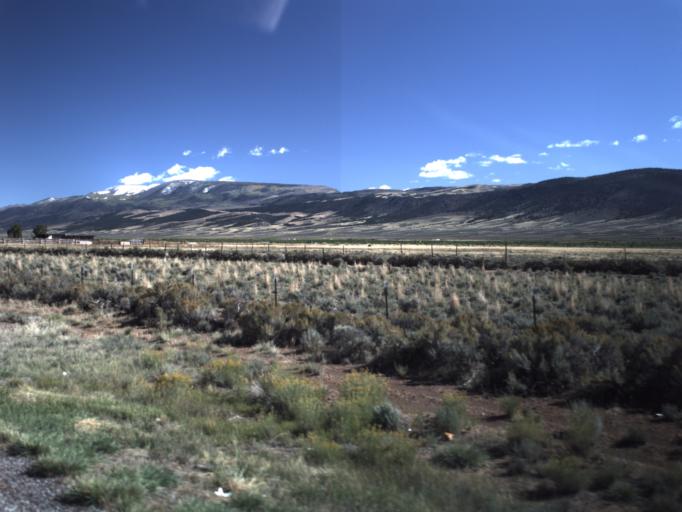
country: US
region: Utah
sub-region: Wayne County
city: Loa
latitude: 38.4217
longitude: -111.9229
